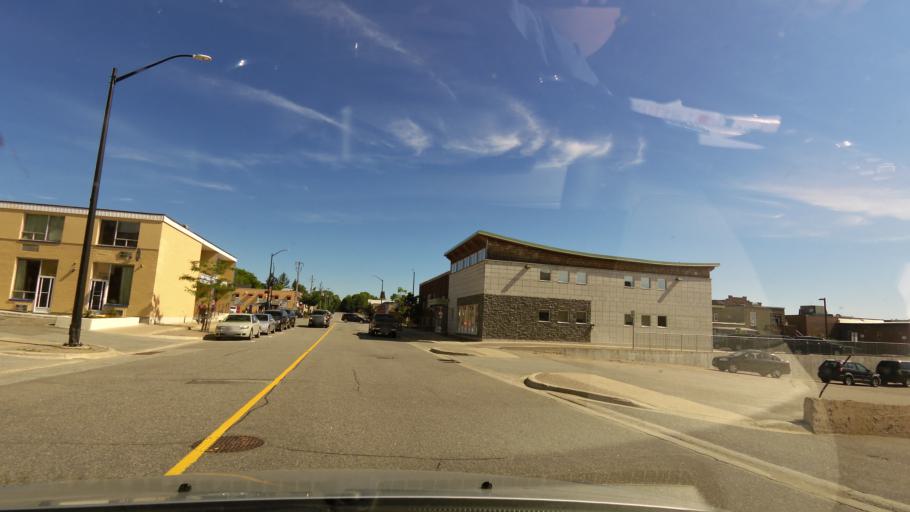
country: CA
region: Ontario
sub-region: Parry Sound District
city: Parry Sound
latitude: 45.3428
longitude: -80.0352
